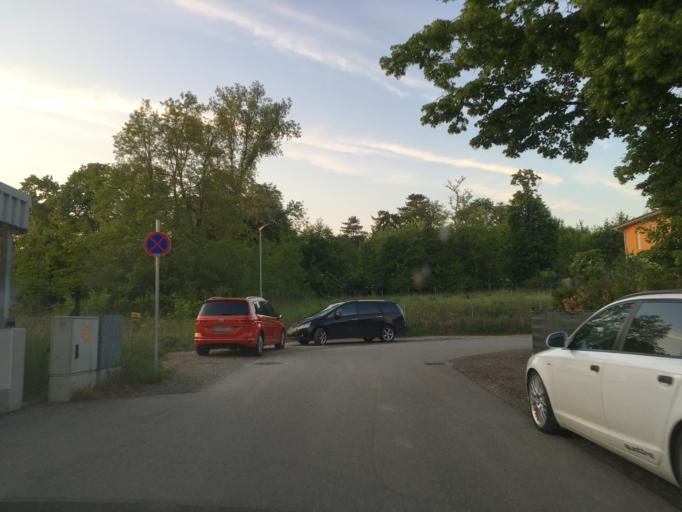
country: AT
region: Lower Austria
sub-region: Politischer Bezirk Korneuburg
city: Stockerau
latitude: 48.3909
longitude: 16.1977
